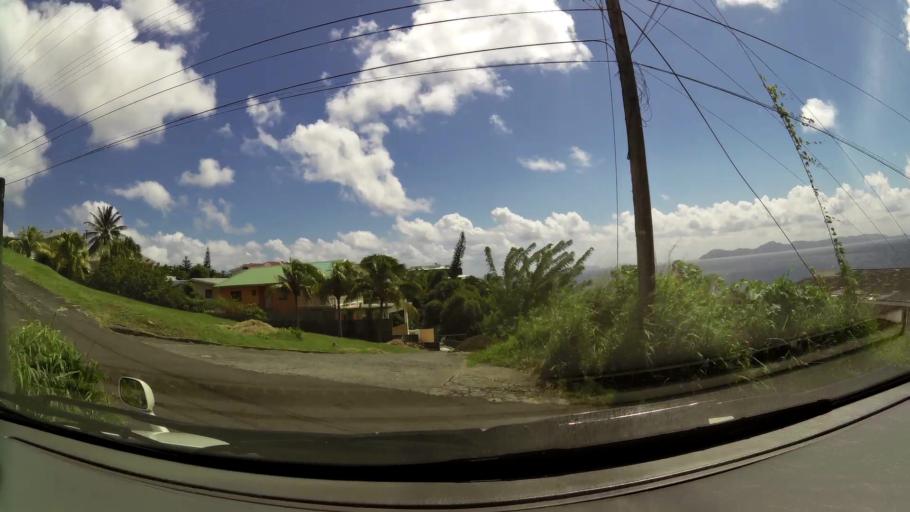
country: VC
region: Saint George
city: Kingstown
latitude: 13.1400
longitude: -61.2274
